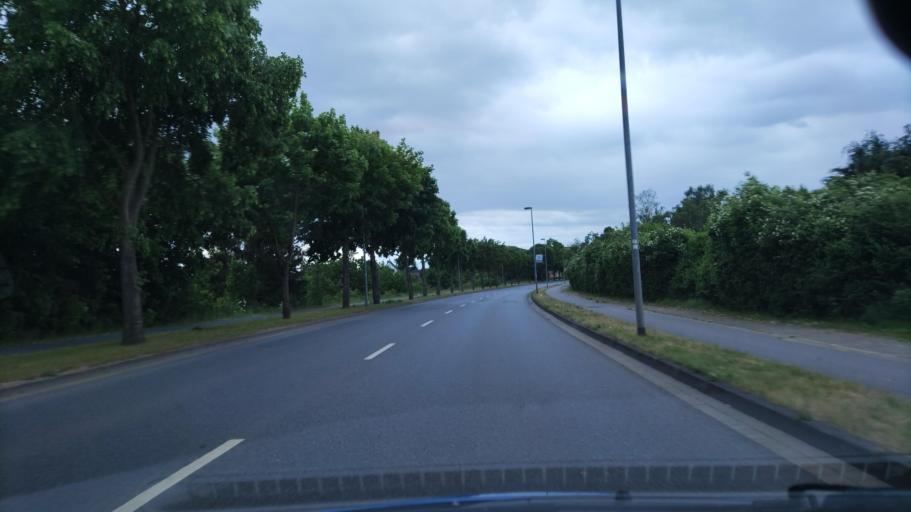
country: DE
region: Mecklenburg-Vorpommern
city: Parchim
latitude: 53.4292
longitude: 11.8643
